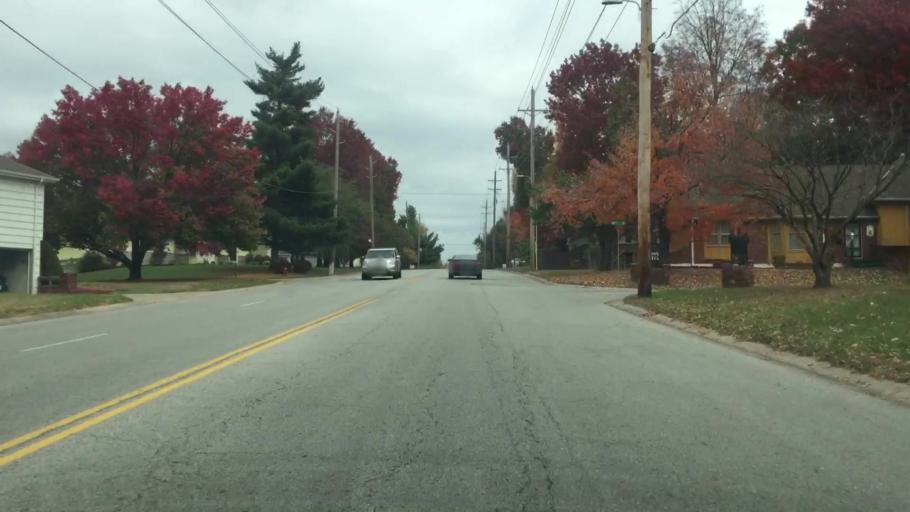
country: US
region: Missouri
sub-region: Jackson County
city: Raytown
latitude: 39.0090
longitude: -94.4449
